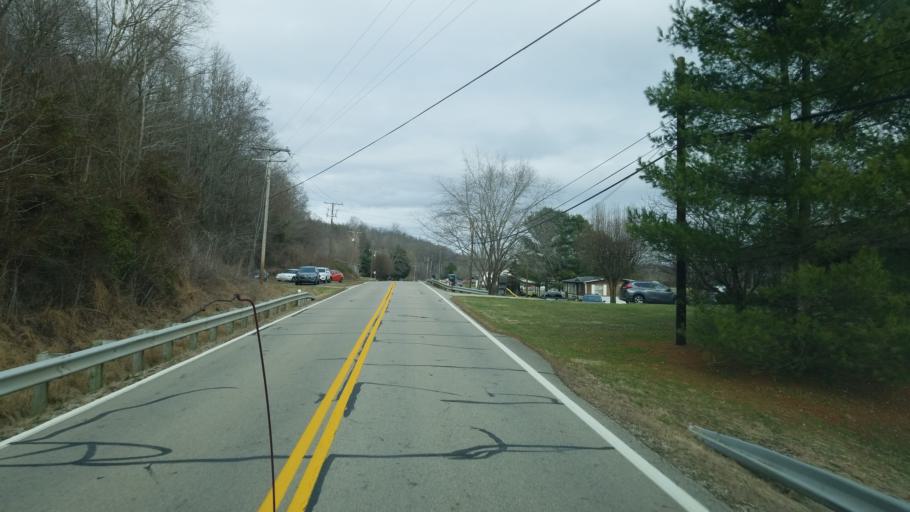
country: US
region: Ohio
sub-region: Scioto County
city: West Portsmouth
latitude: 38.6558
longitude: -83.1316
